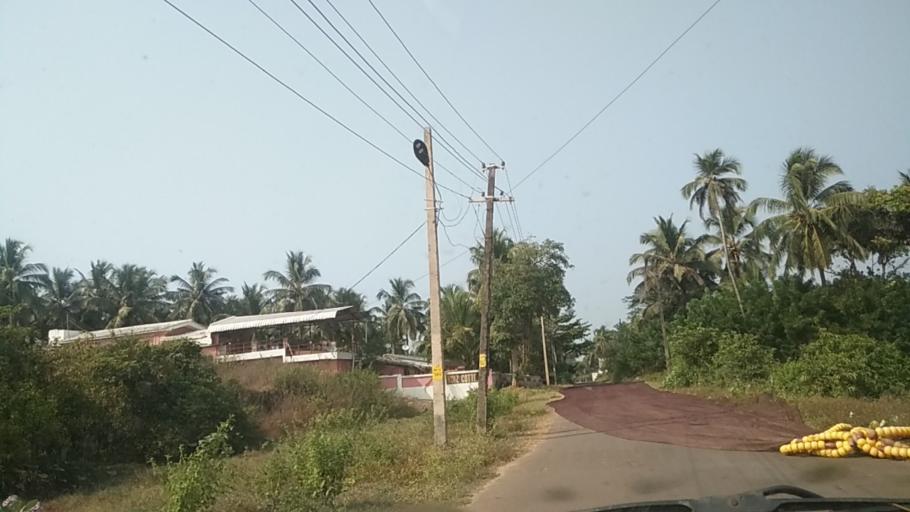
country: IN
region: Goa
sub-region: South Goa
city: Colva
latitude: 15.2862
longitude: 73.9122
